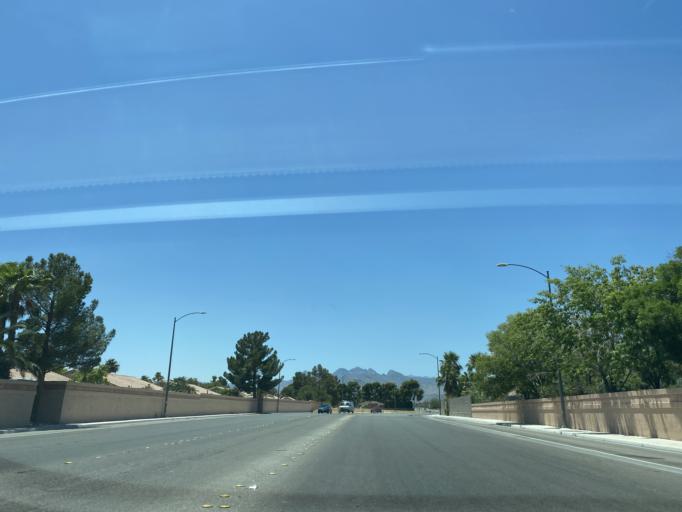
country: US
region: Nevada
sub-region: Clark County
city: Las Vegas
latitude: 36.2318
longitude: -115.2135
